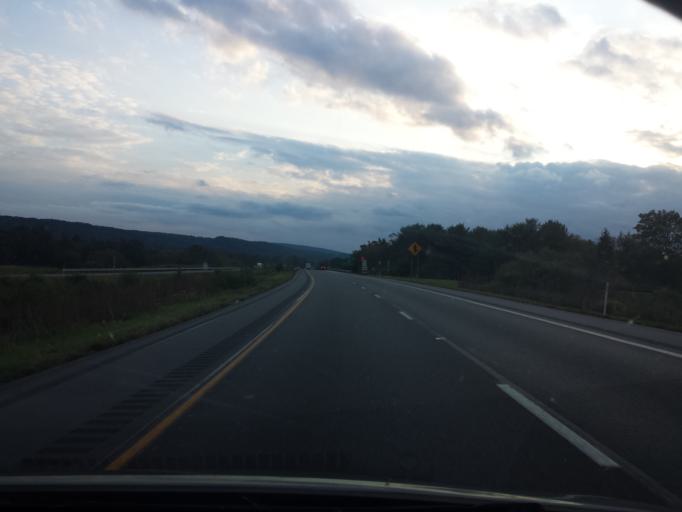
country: US
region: Pennsylvania
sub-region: Northumberland County
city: Riverside
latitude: 40.9978
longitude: -76.6420
